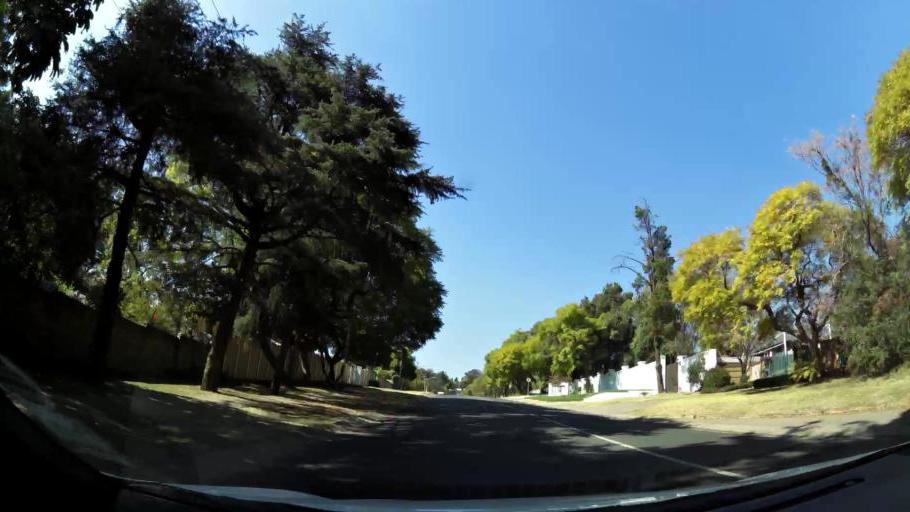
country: ZA
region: Gauteng
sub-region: City of Tshwane Metropolitan Municipality
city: Pretoria
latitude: -25.7839
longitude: 28.2341
